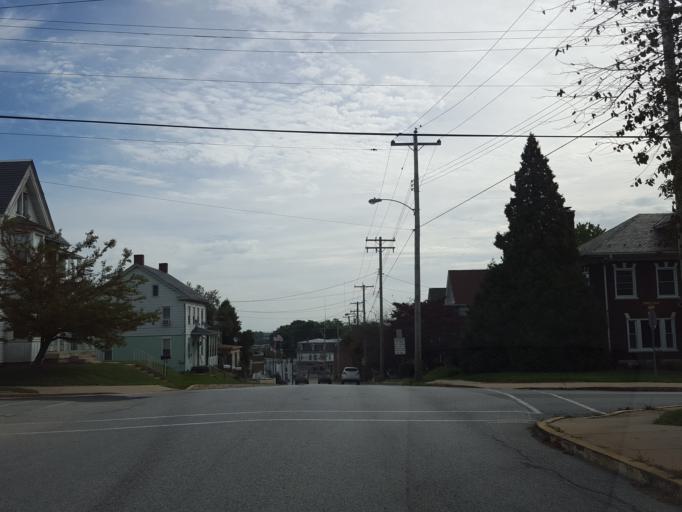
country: US
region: Pennsylvania
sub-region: York County
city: Red Lion
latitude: 39.9022
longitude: -76.6106
